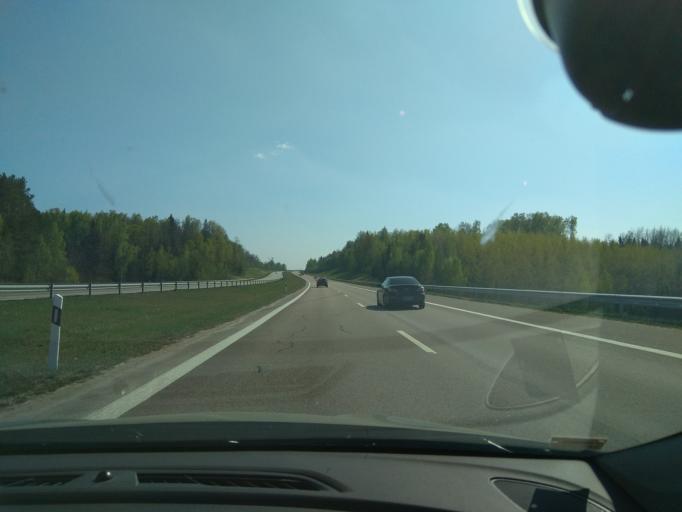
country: LT
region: Vilnius County
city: Ukmerge
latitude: 55.2194
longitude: 24.8163
